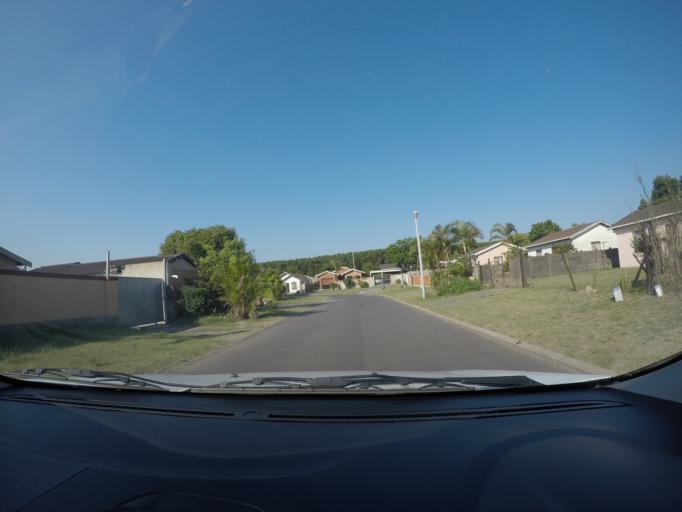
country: ZA
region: KwaZulu-Natal
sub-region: uThungulu District Municipality
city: Richards Bay
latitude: -28.7131
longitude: 32.0398
